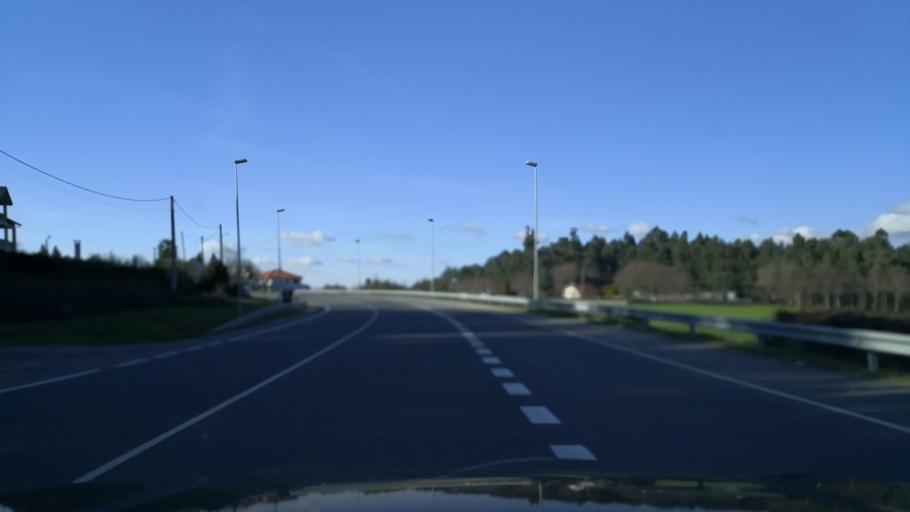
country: ES
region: Galicia
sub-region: Provincia de Pontevedra
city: Silleda
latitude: 42.7203
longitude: -8.2848
